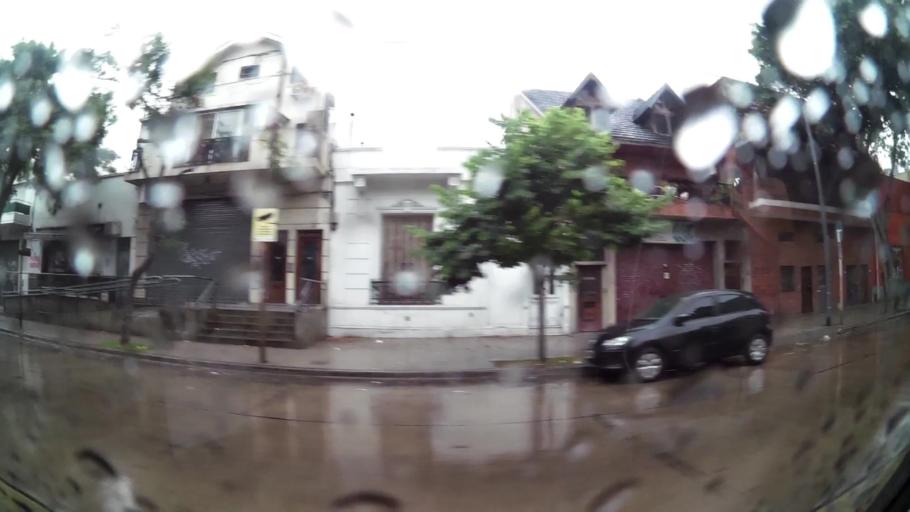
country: AR
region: Buenos Aires
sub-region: Partido de Avellaneda
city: Avellaneda
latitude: -34.6443
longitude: -58.3689
